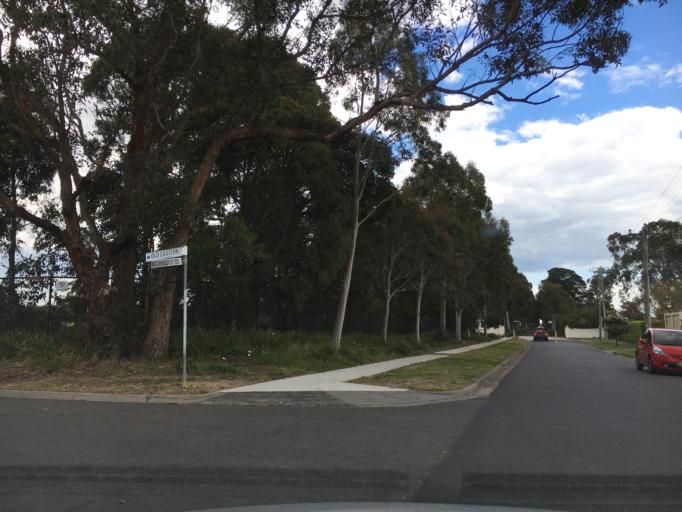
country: AU
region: Victoria
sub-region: Monash
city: Oakleigh South
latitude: -37.9134
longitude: 145.0985
